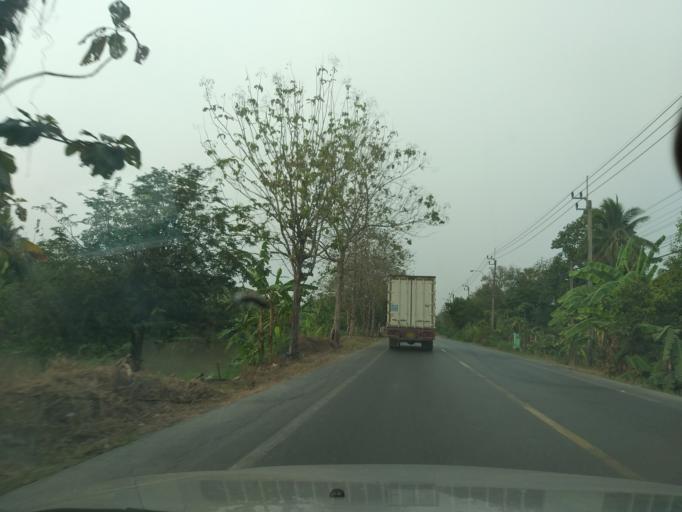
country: TH
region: Bangkok
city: Nong Chok
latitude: 13.8905
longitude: 100.8869
